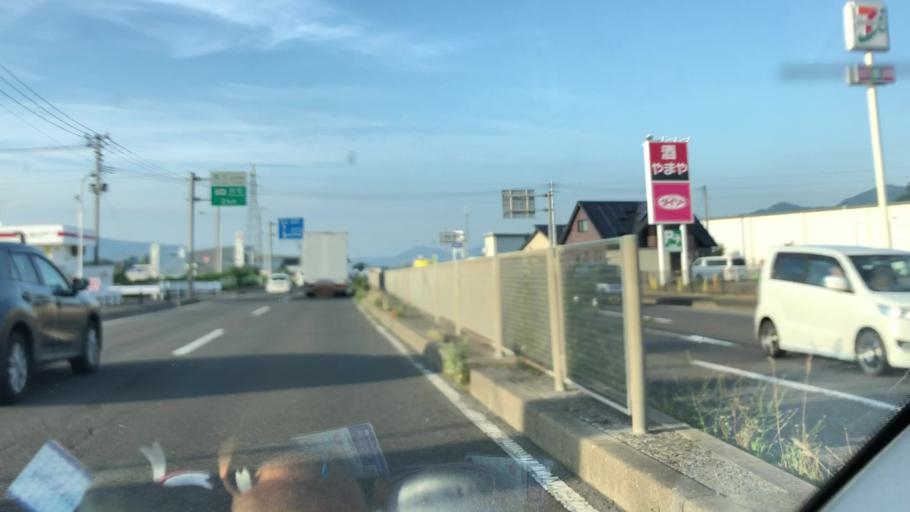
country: JP
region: Miyagi
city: Shiroishi
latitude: 38.0226
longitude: 140.6246
